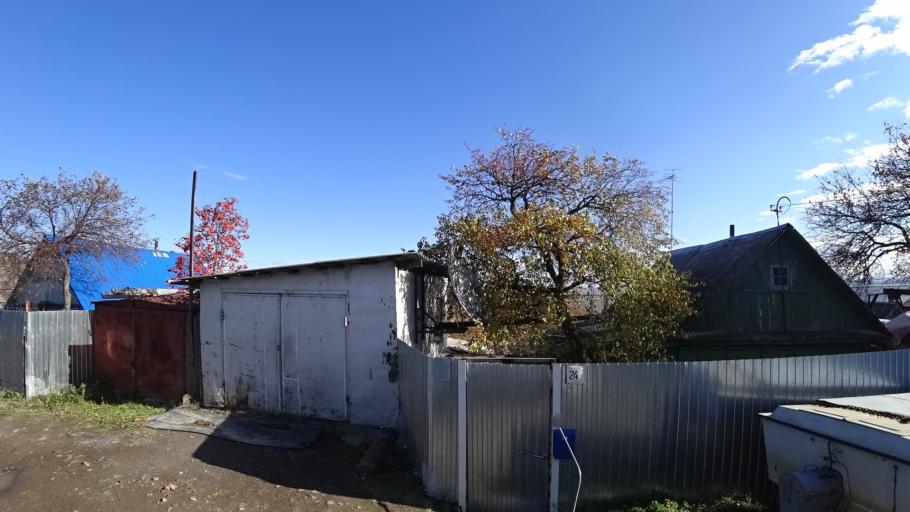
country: RU
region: Khabarovsk Krai
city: Amursk
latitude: 50.2322
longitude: 136.9195
